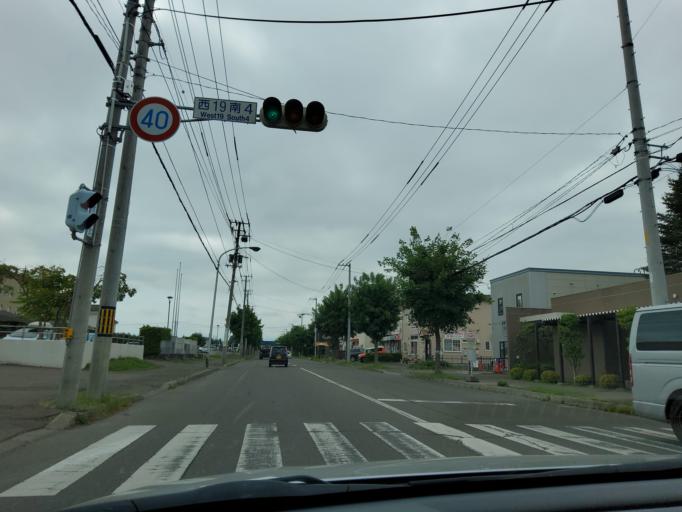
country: JP
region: Hokkaido
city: Obihiro
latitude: 42.9134
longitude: 143.1550
